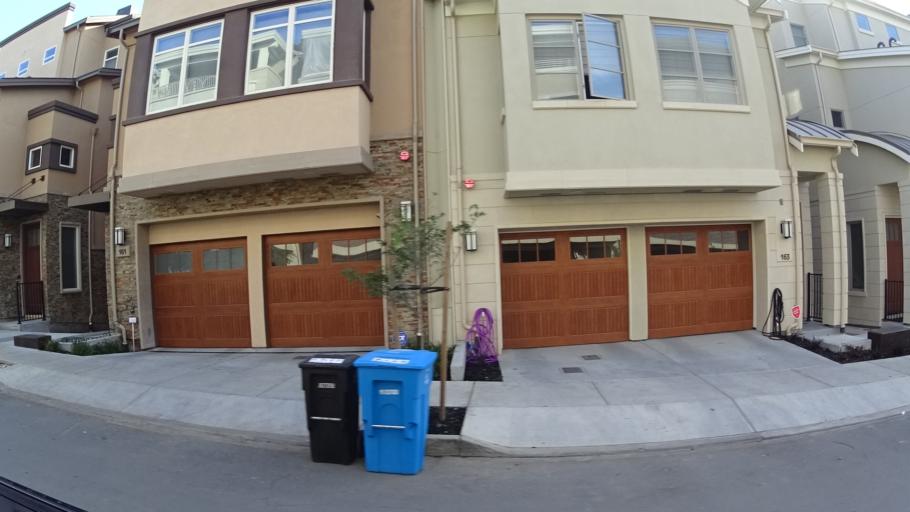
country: US
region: California
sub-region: San Mateo County
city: Daly City
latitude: 37.7154
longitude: -122.4761
